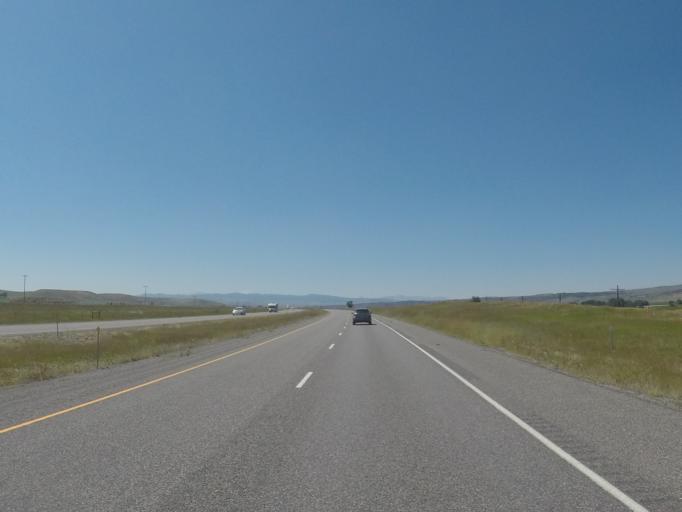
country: US
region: Montana
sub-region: Park County
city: Livingston
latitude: 45.7031
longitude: -110.3340
